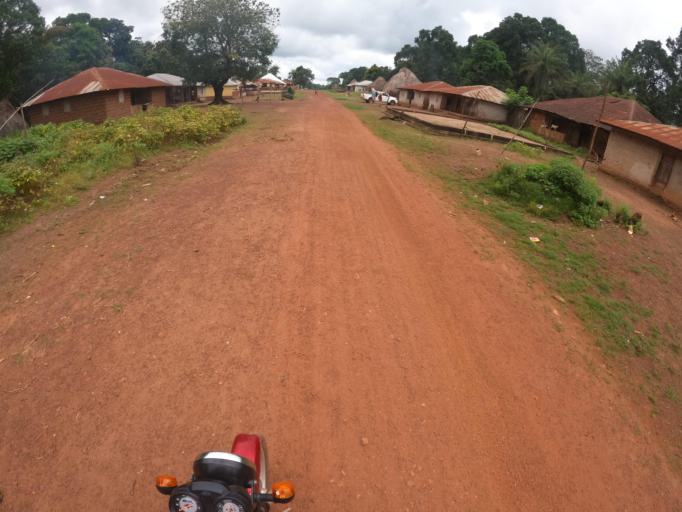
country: SL
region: Northern Province
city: Kamakwie
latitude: 9.5109
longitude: -12.2679
